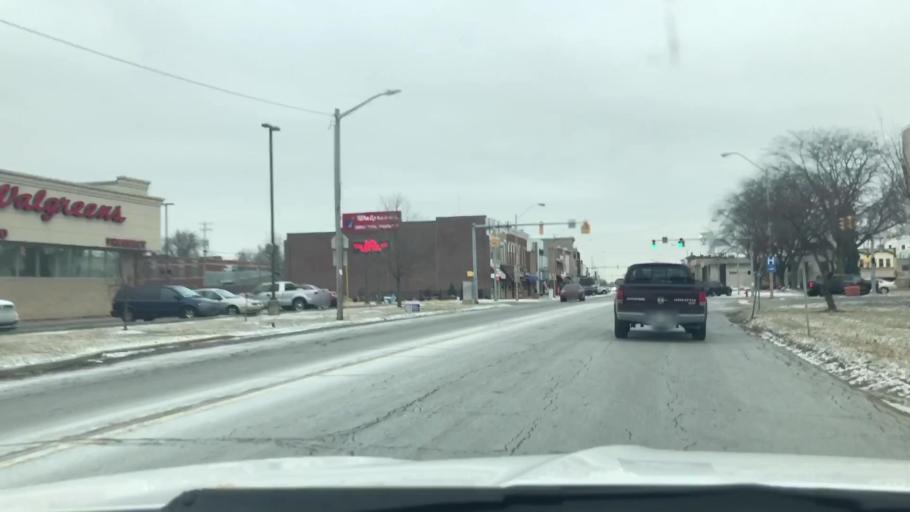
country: US
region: Indiana
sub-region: Fulton County
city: Rochester
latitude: 41.0643
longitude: -86.2160
